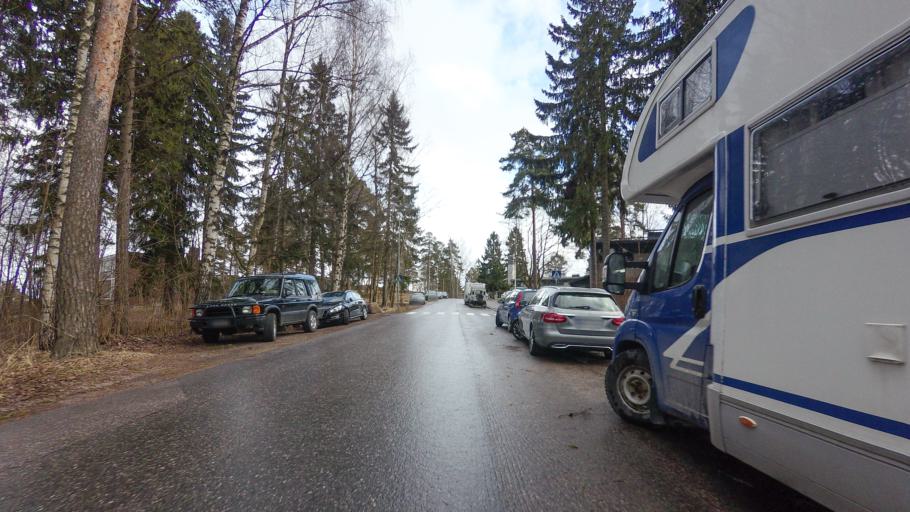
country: FI
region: Uusimaa
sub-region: Helsinki
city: Vantaa
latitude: 60.1940
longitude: 25.0692
